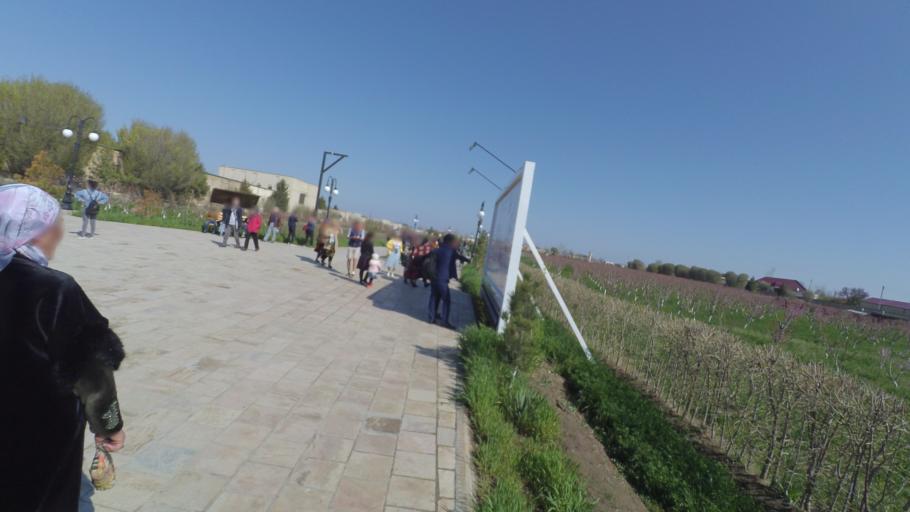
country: UZ
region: Bukhara
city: Kogon
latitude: 39.8017
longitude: 64.5387
